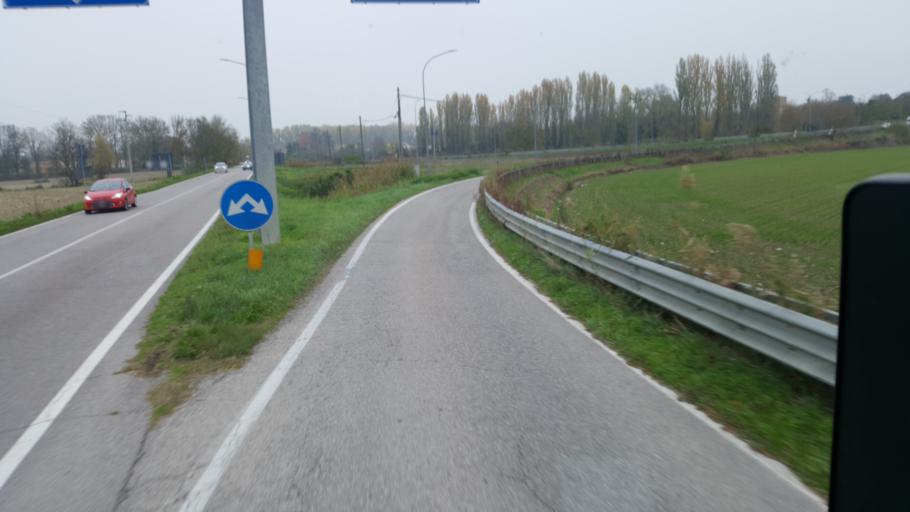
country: IT
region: Veneto
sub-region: Provincia di Rovigo
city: Ficarolo
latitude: 44.9456
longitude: 11.4163
